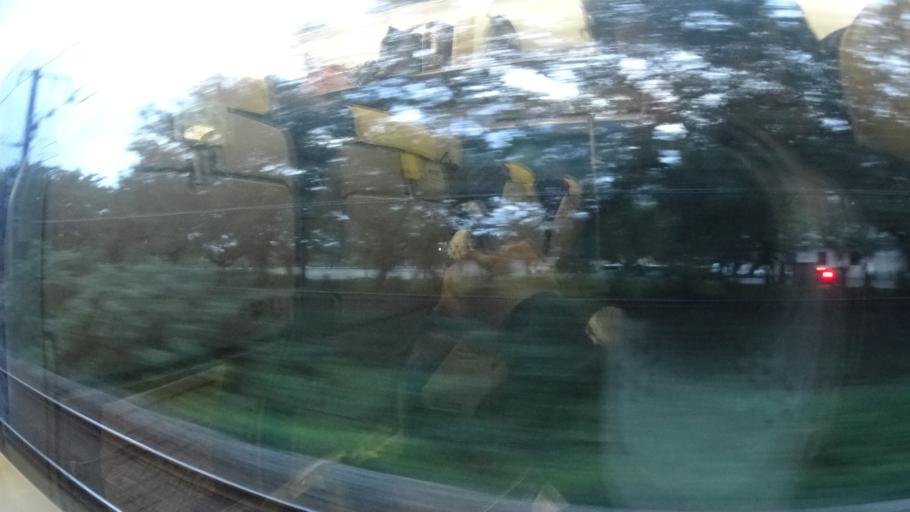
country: JP
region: Niigata
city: Shibata
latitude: 37.9498
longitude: 139.3406
